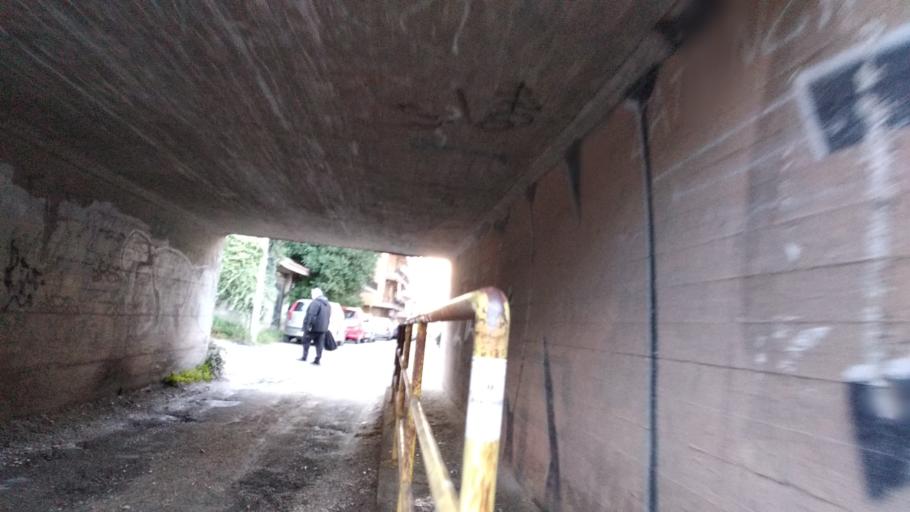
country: IT
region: Calabria
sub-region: Provincia di Catanzaro
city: Barone
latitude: 38.8283
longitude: 16.6254
